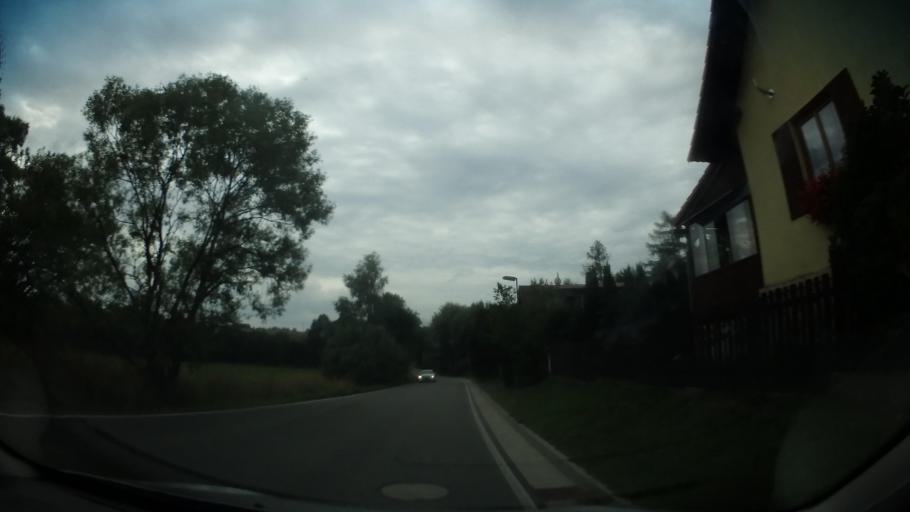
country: CZ
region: Pardubicky
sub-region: Okres Chrudim
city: Nasavrky
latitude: 49.7999
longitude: 15.7745
